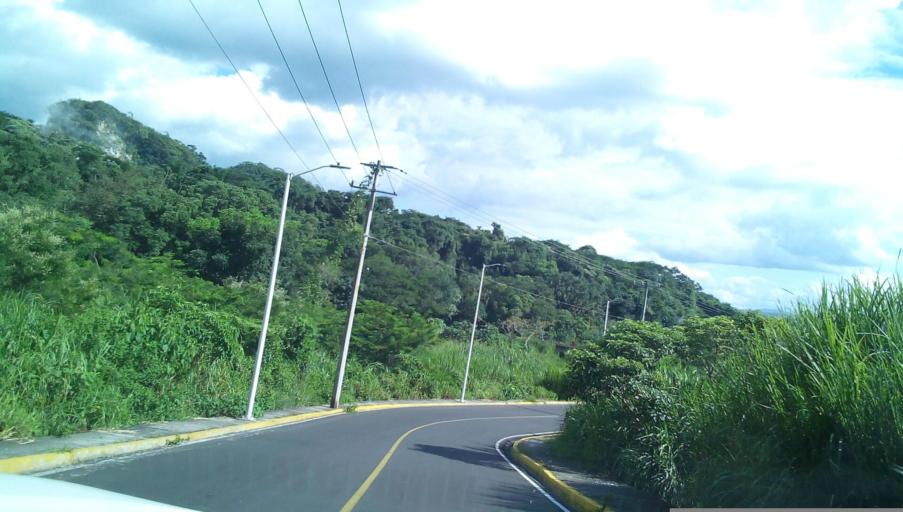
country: MX
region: Veracruz
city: Cordoba
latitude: 18.8948
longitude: -96.9202
